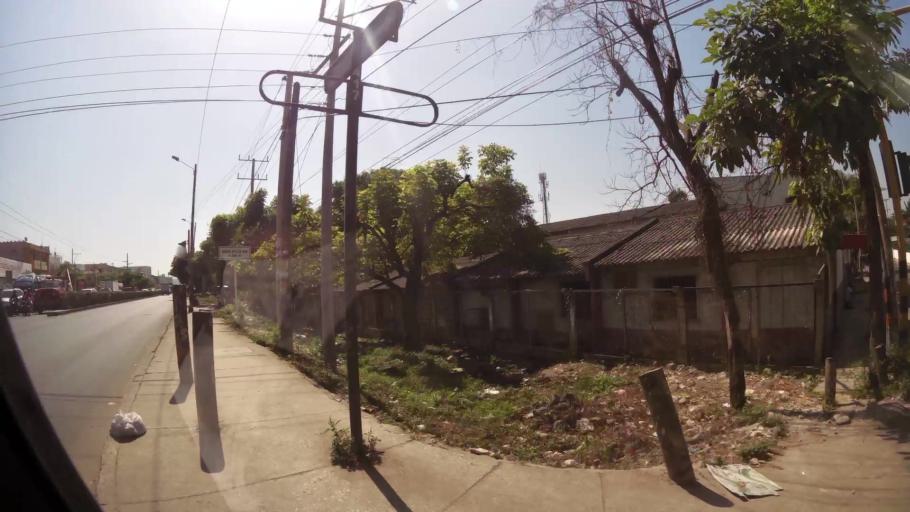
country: CO
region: Bolivar
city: Cartagena
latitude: 10.3858
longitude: -75.4713
